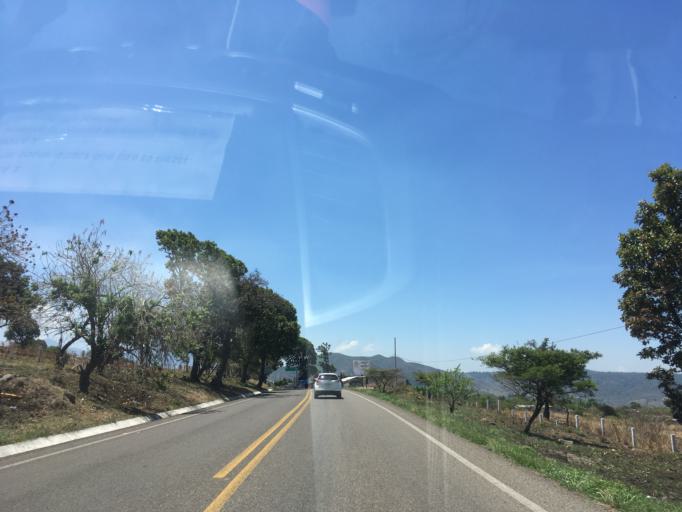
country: MX
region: Michoacan
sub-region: Zitacuaro
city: Puentecillas (Tercera Manzana de Zirahuato)
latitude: 19.4868
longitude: -100.4469
